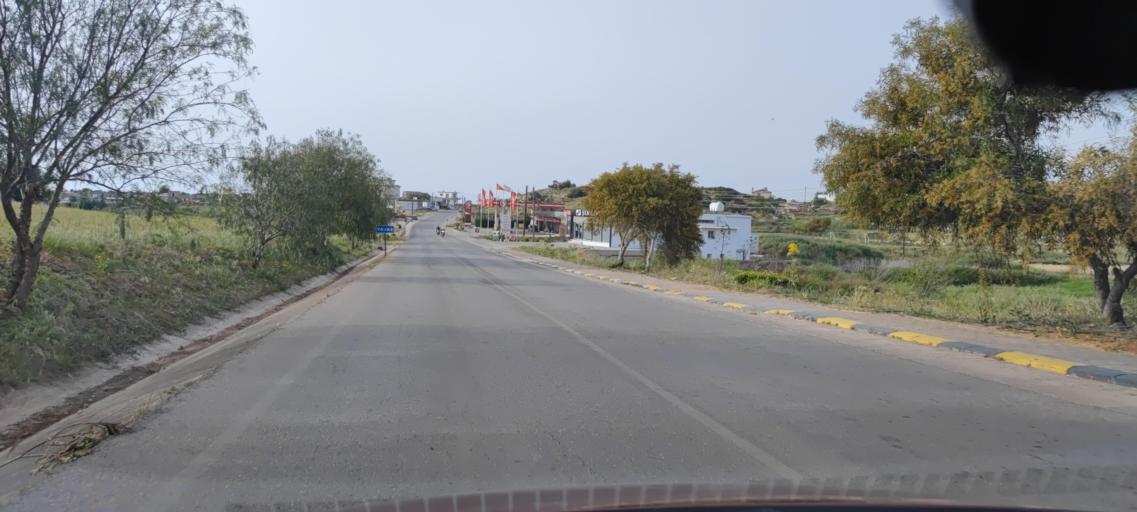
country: CY
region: Ammochostos
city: Leonarisso
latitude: 35.5047
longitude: 34.1614
